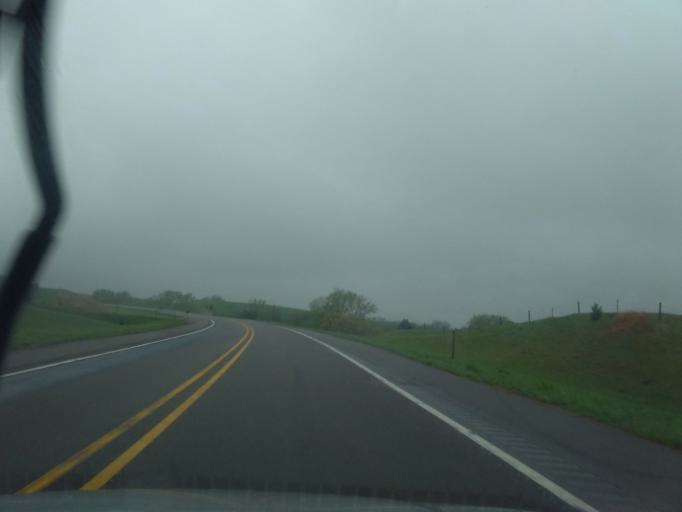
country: US
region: Nebraska
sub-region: Madison County
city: Norfolk
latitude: 42.1046
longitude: -97.3117
